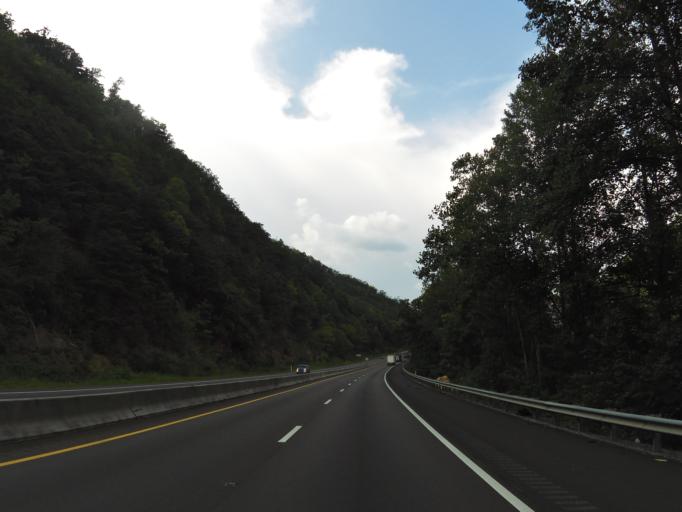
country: US
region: Tennessee
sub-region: Cocke County
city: Newport
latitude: 35.8256
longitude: -83.1834
